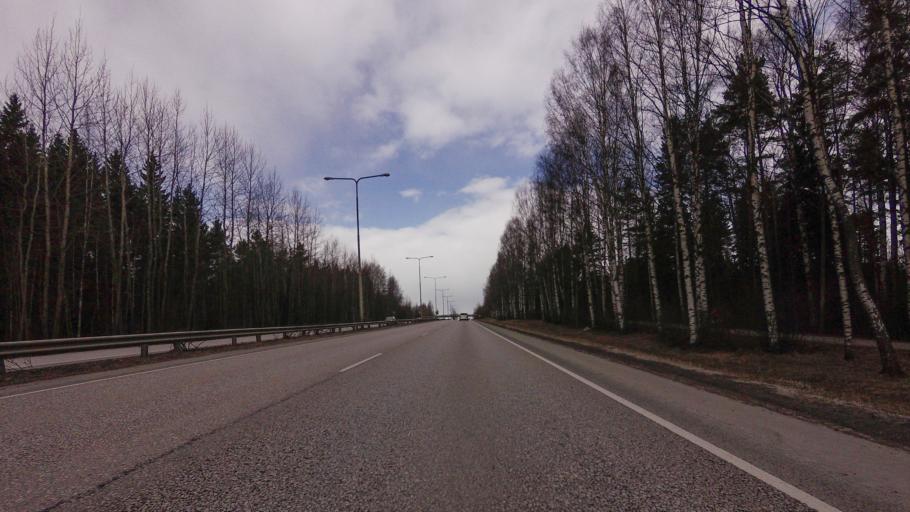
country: FI
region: Uusimaa
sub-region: Helsinki
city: Helsinki
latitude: 60.2306
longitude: 24.9044
